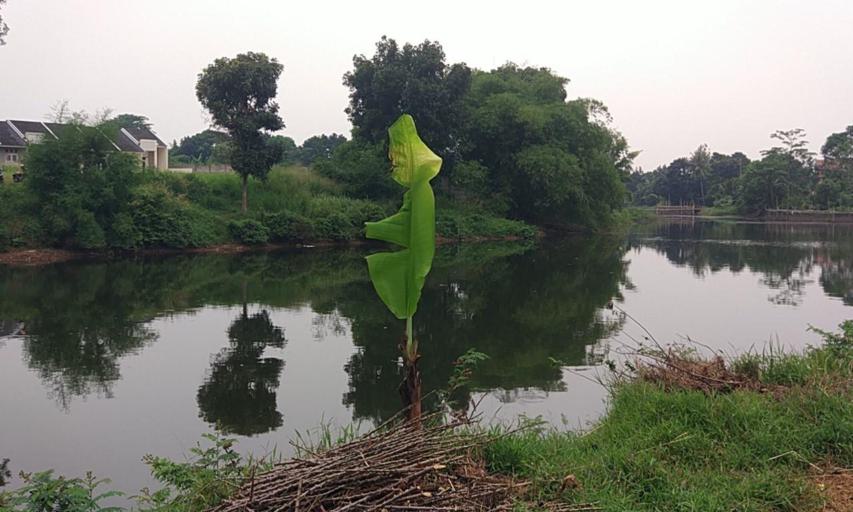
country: ID
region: West Java
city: Parung
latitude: -6.4960
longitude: 106.7660
